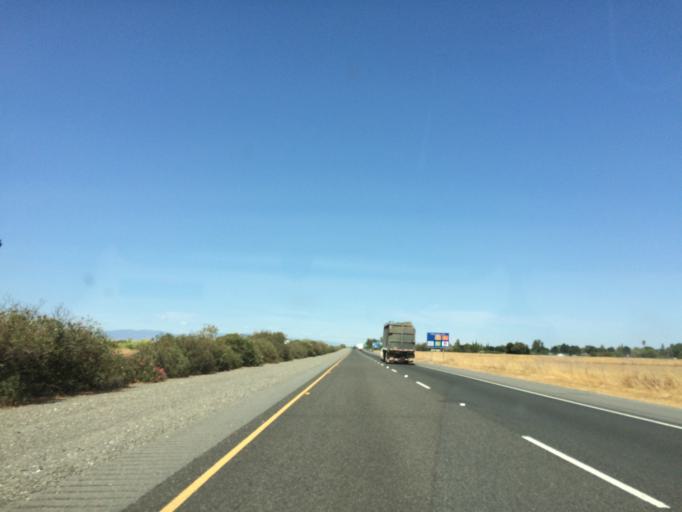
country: US
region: California
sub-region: Glenn County
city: Willows
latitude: 39.5057
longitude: -122.2036
